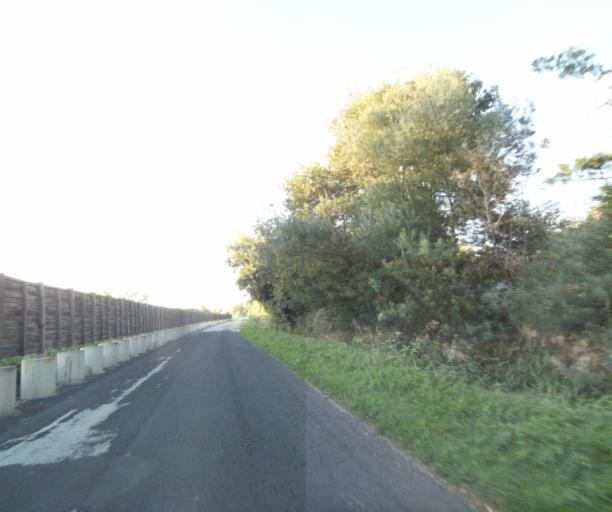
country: FR
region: Languedoc-Roussillon
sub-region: Departement des Pyrenees-Orientales
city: Sant Andreu de Sureda
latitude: 42.5718
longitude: 2.9980
